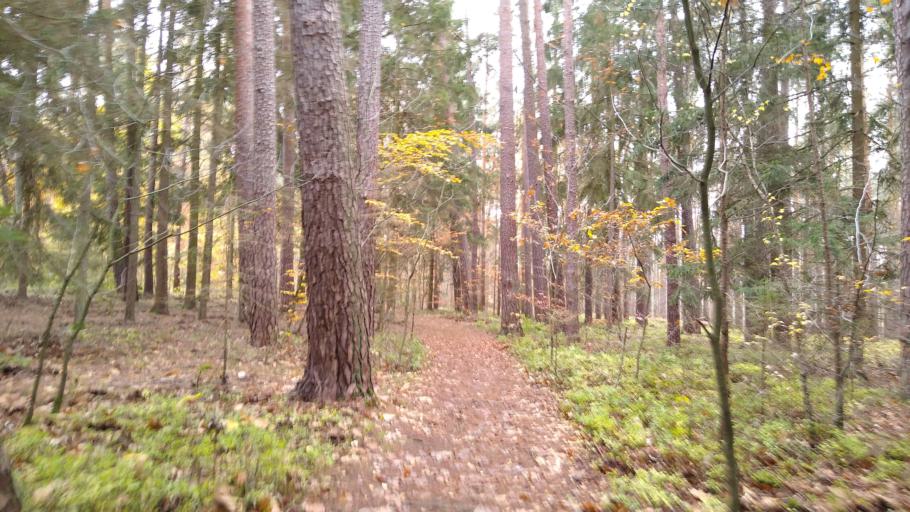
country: DE
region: Bavaria
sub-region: Regierungsbezirk Mittelfranken
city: Kalchreuth
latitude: 49.5473
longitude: 11.1138
